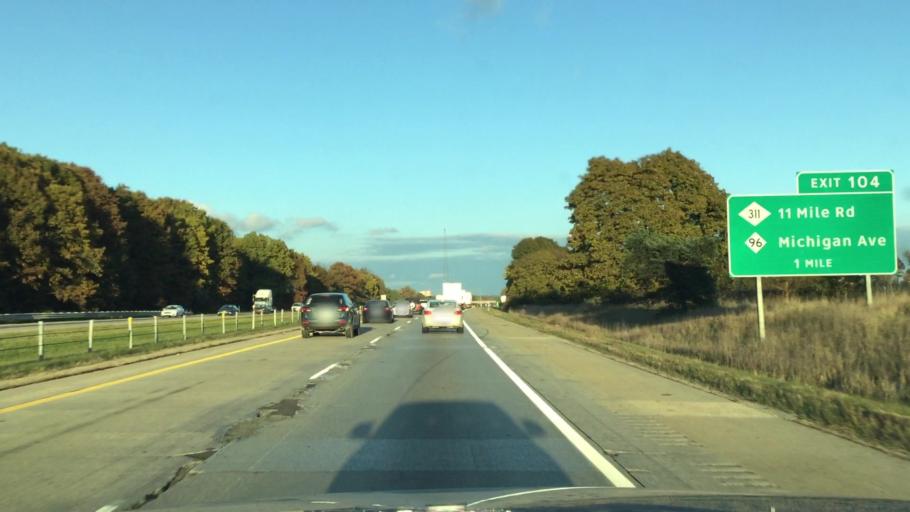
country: US
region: Michigan
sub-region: Calhoun County
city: Brownlee Park
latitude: 42.2948
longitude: -85.1005
